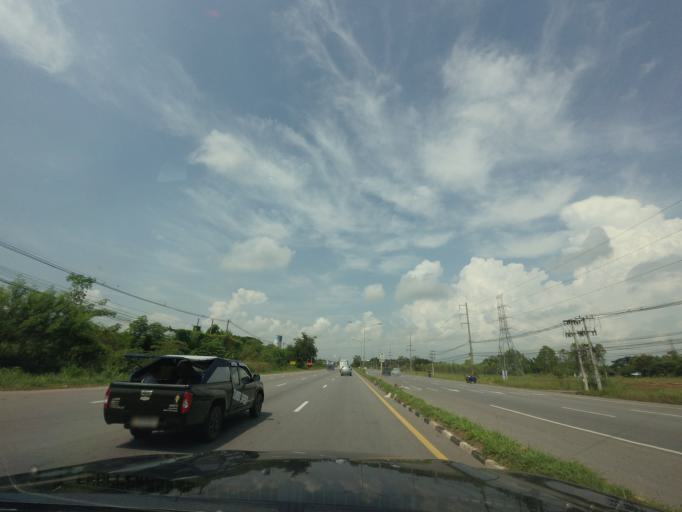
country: TH
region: Khon Kaen
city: Khon Kaen
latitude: 16.4508
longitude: 102.7467
